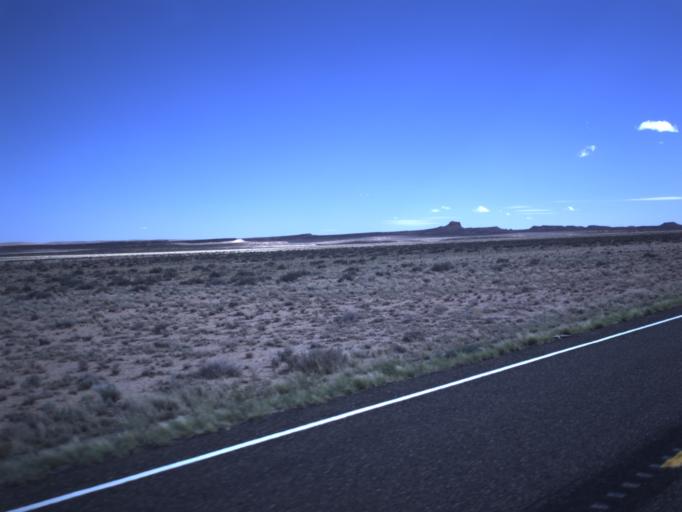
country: US
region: Utah
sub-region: Emery County
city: Ferron
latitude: 38.2888
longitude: -110.6651
